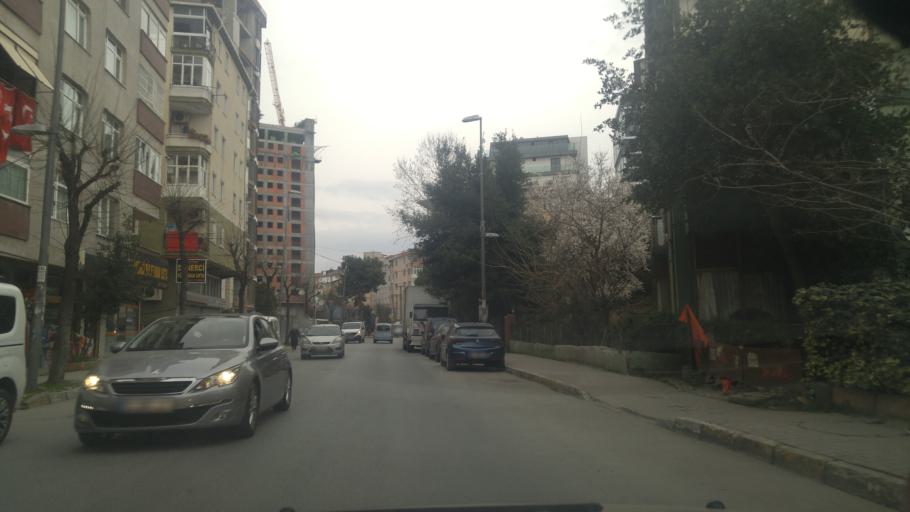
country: TR
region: Istanbul
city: Mahmutbey
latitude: 40.9958
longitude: 28.7666
